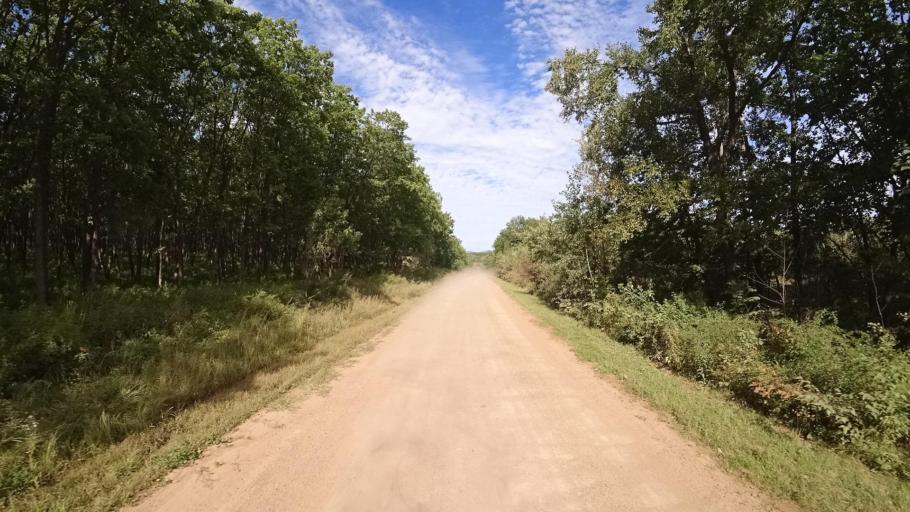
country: RU
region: Primorskiy
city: Yakovlevka
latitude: 44.3842
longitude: 133.5362
